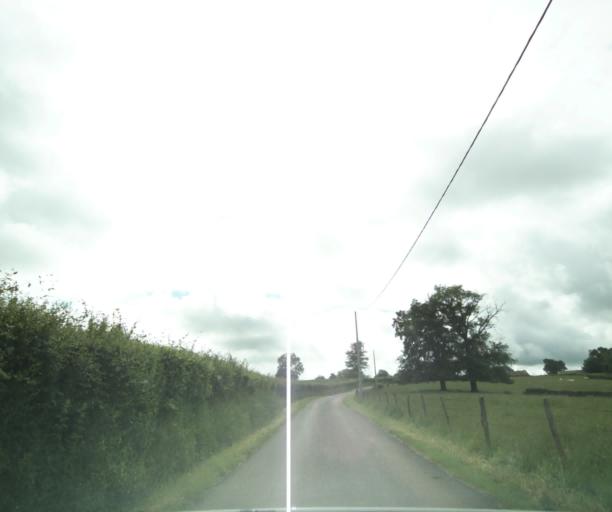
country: FR
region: Bourgogne
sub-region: Departement de Saone-et-Loire
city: Charolles
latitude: 46.4213
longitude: 4.3073
